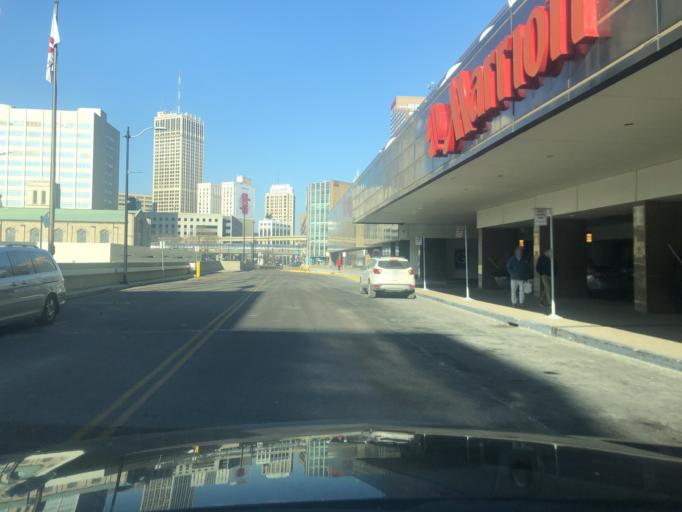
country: US
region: Michigan
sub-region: Wayne County
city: Detroit
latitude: 42.3285
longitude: -83.0408
